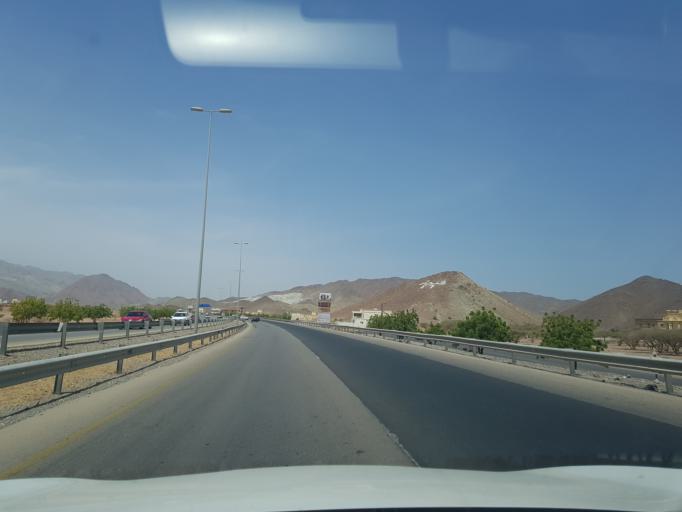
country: OM
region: Muhafazat ad Dakhiliyah
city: Bidbid
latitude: 23.4664
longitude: 58.1467
